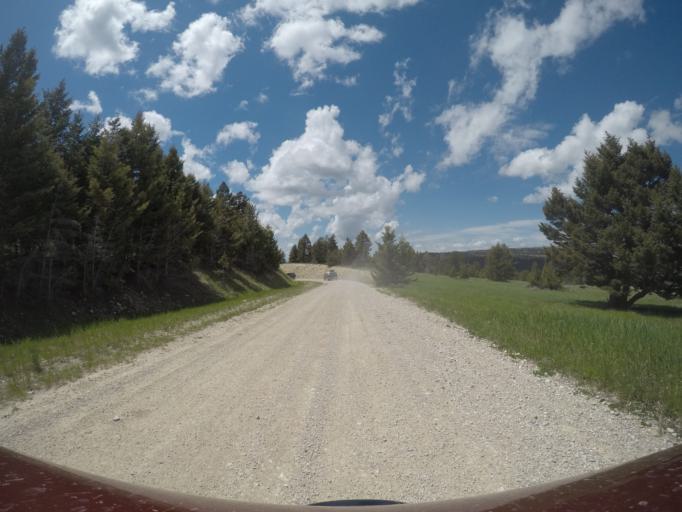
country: US
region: Wyoming
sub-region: Big Horn County
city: Lovell
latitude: 45.2022
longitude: -108.5122
